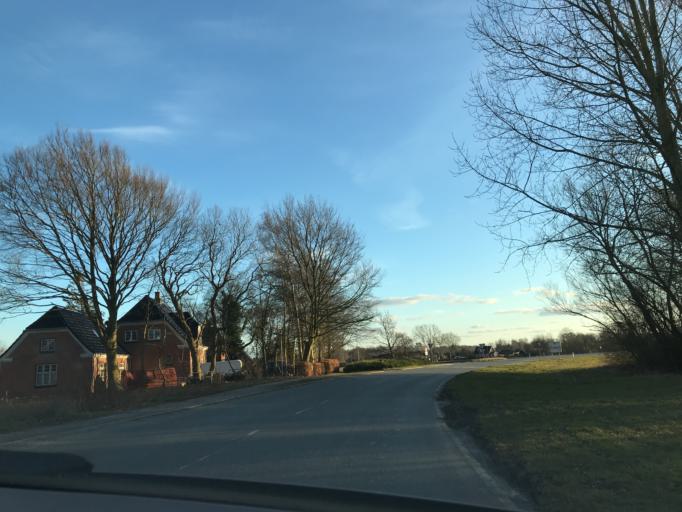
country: DK
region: South Denmark
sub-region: Middelfart Kommune
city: Brenderup
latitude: 55.4878
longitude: 9.9773
